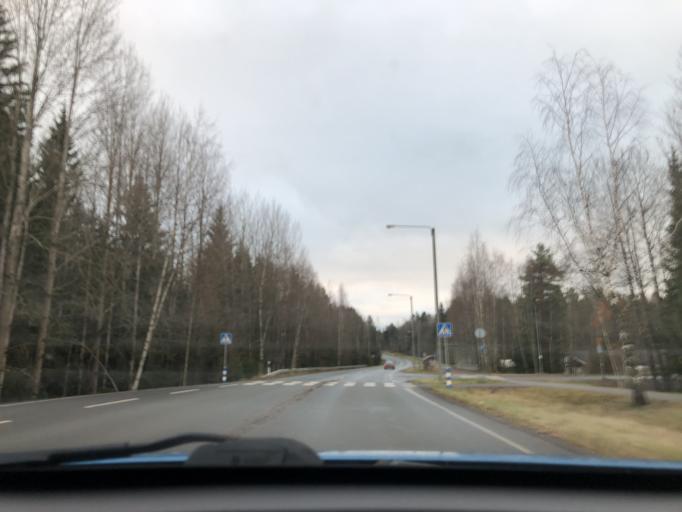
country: FI
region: Pirkanmaa
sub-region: Tampere
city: Kangasala
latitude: 61.5310
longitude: 23.9529
